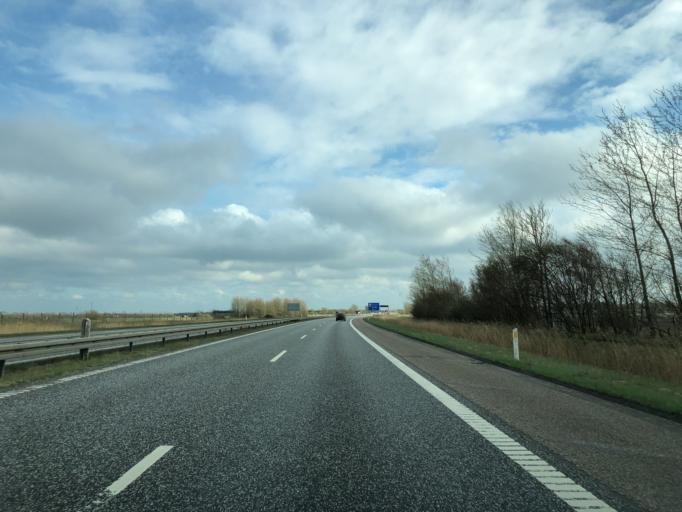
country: DK
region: North Denmark
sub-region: Alborg Kommune
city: Vestbjerg
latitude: 57.1019
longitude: 9.9639
